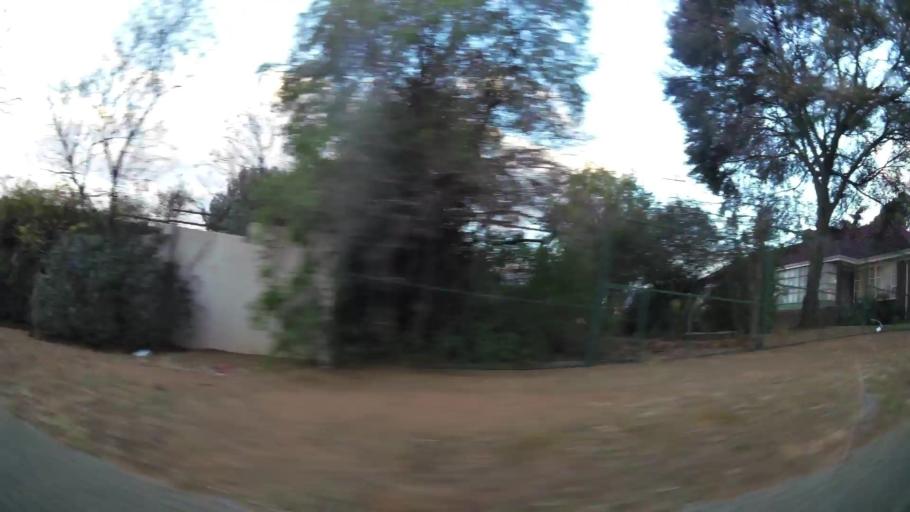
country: ZA
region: Gauteng
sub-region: West Rand District Municipality
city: Krugersdorp
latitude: -26.0765
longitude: 27.7783
